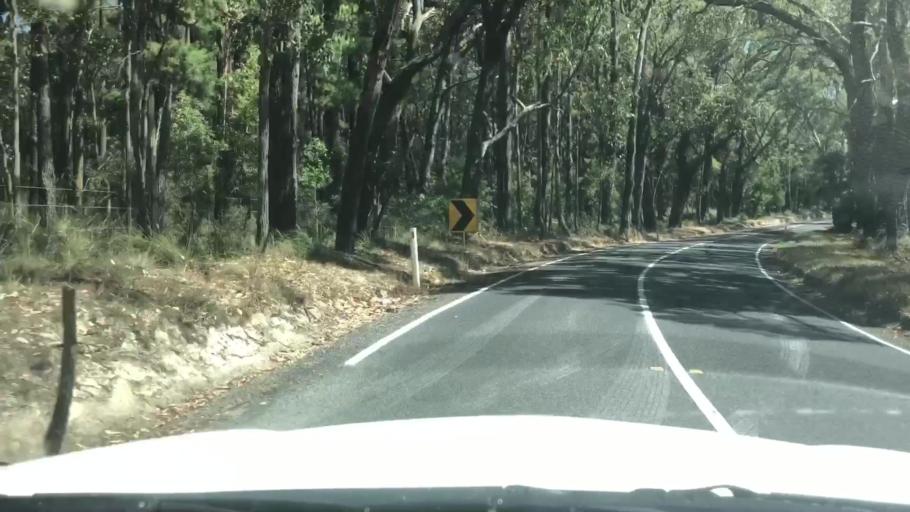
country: AU
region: Victoria
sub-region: Yarra Ranges
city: Macclesfield
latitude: -37.8503
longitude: 145.4876
